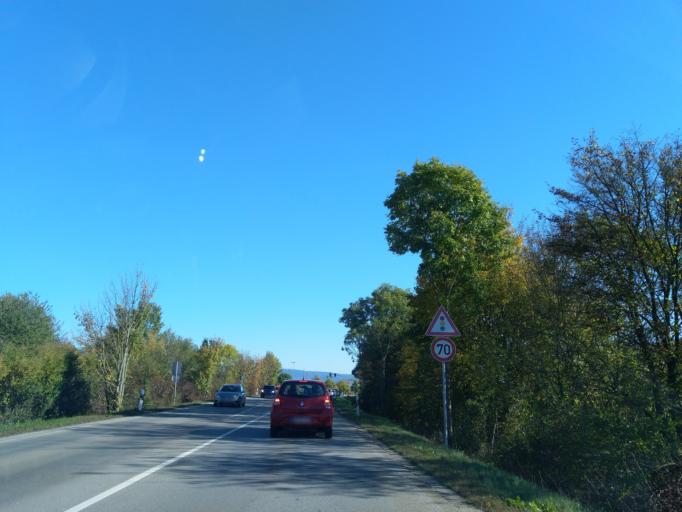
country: DE
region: Bavaria
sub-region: Lower Bavaria
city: Plattling
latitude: 48.7862
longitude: 12.8925
